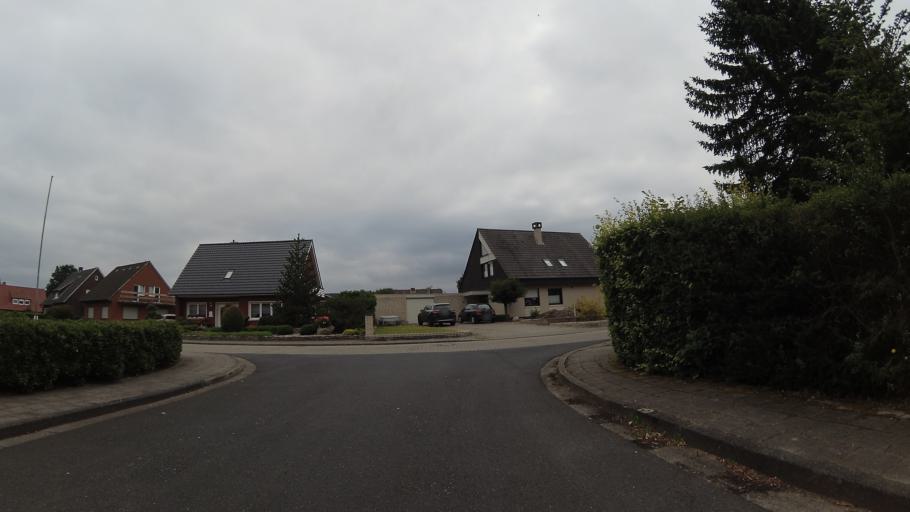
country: DE
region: Lower Saxony
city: Fresenburg
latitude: 52.8822
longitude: 7.3095
